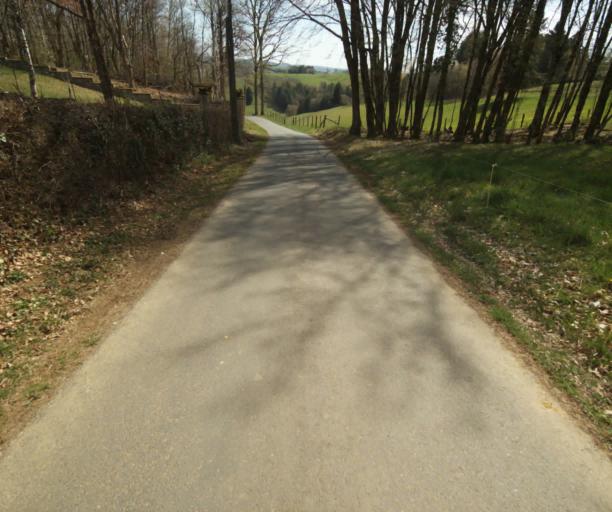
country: FR
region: Limousin
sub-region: Departement de la Correze
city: Seilhac
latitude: 45.3906
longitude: 1.7706
